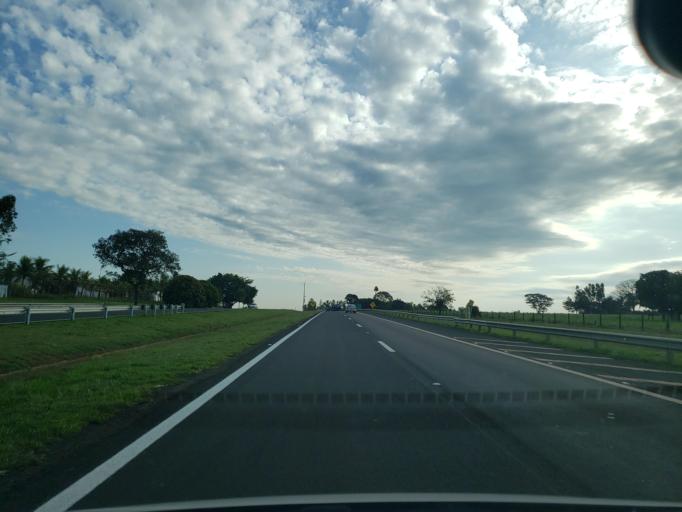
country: BR
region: Sao Paulo
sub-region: Guararapes
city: Guararapes
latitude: -21.2086
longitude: -50.6615
